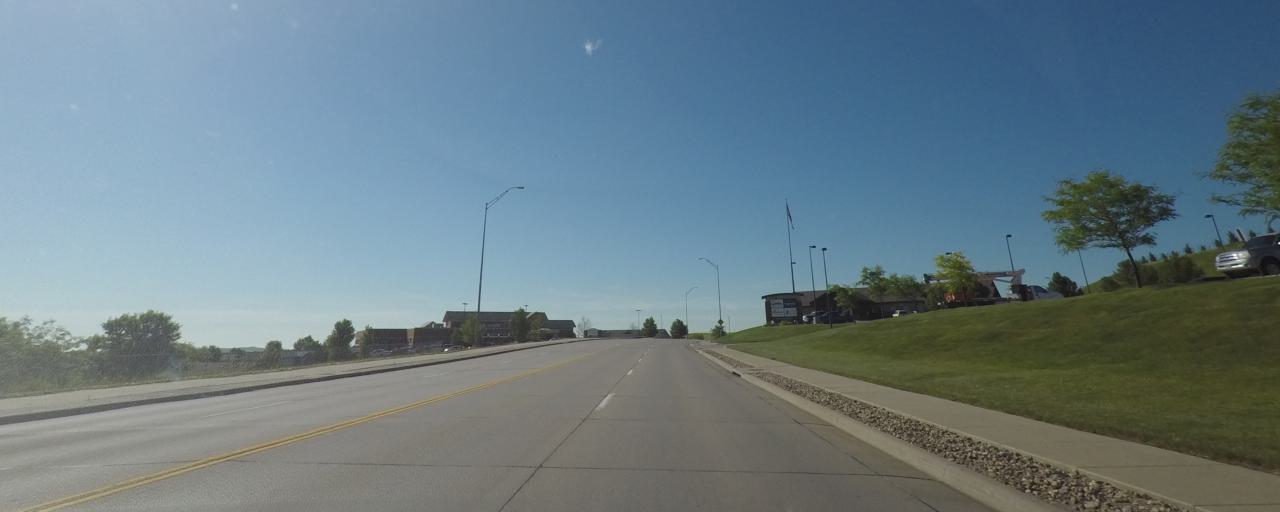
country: US
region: South Dakota
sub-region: Pennington County
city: Rapid City
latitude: 44.0455
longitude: -103.2206
